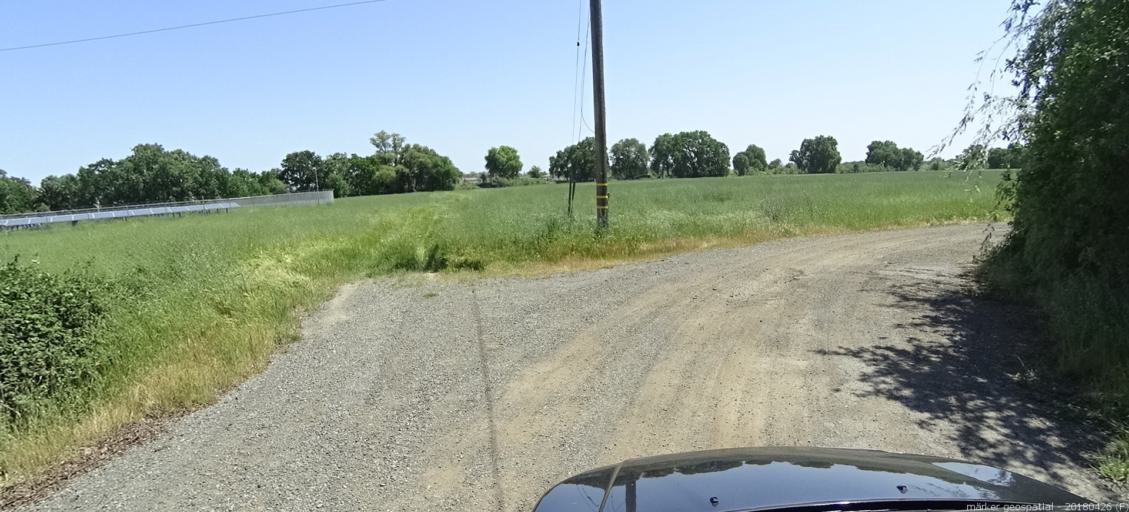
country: US
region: California
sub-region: Yolo County
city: West Sacramento
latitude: 38.5417
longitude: -121.5417
